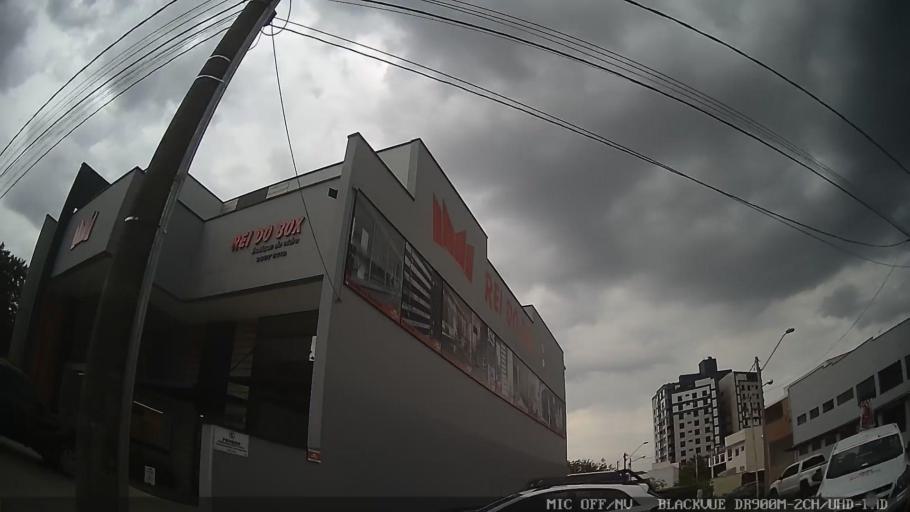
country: BR
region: Sao Paulo
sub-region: Amparo
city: Amparo
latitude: -22.6984
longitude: -46.7597
